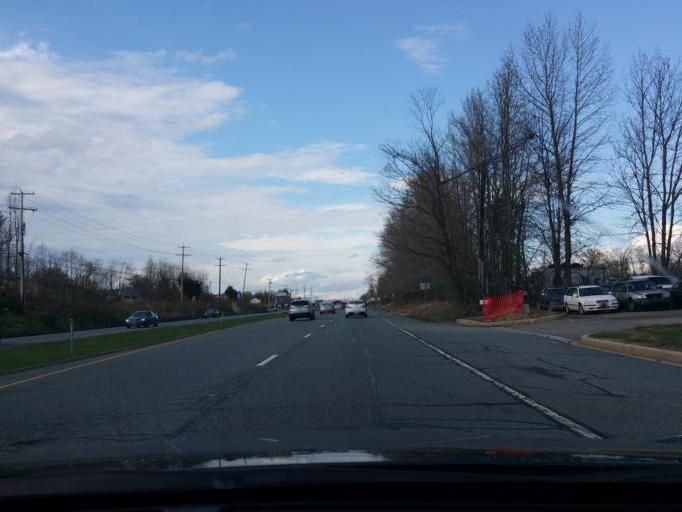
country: US
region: Maryland
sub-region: Harford County
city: Havre de Grace
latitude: 39.5417
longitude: -76.1099
